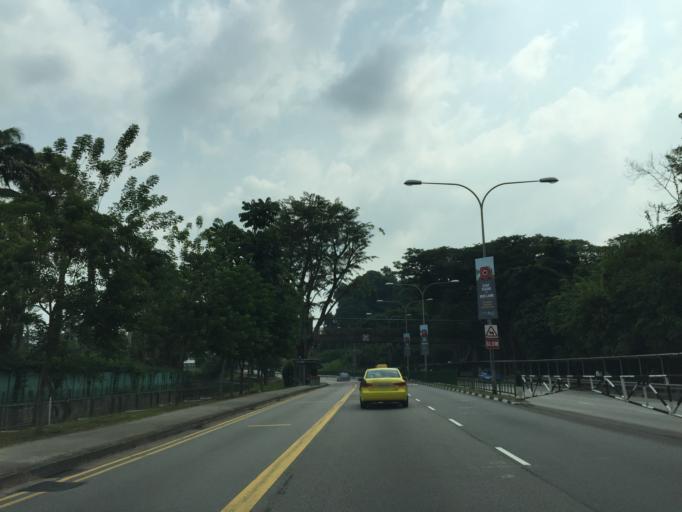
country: SG
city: Singapore
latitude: 1.3326
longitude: 103.8383
